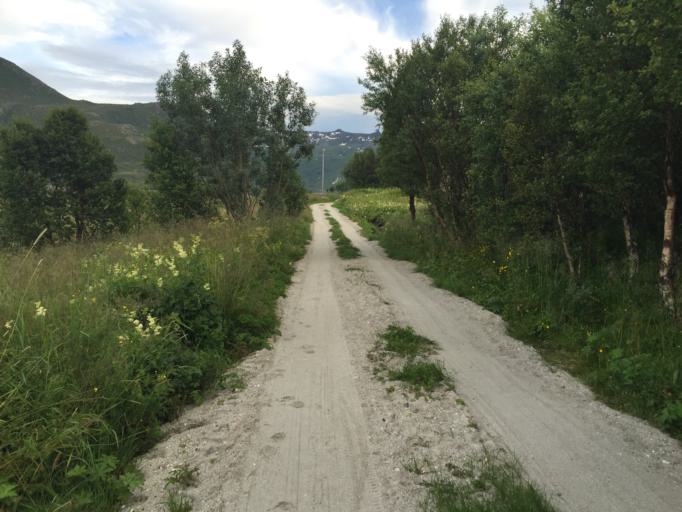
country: NO
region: Nordland
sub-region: Vagan
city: Kabelvag
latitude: 68.3292
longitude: 14.3957
